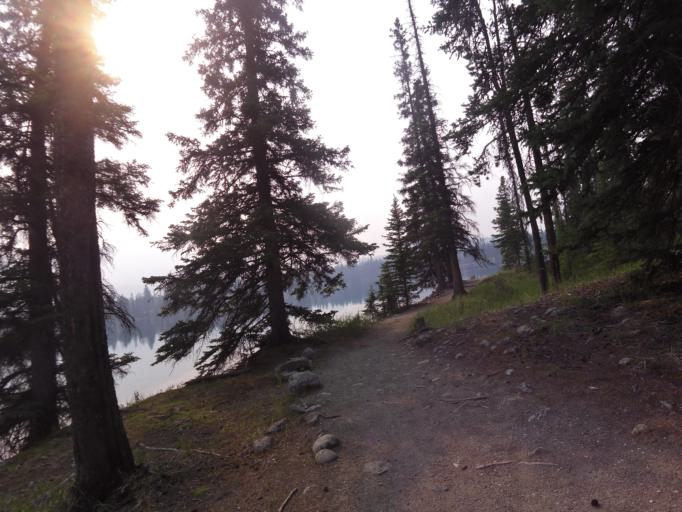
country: CA
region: Alberta
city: Jasper Park Lodge
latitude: 52.8830
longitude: -118.0637
